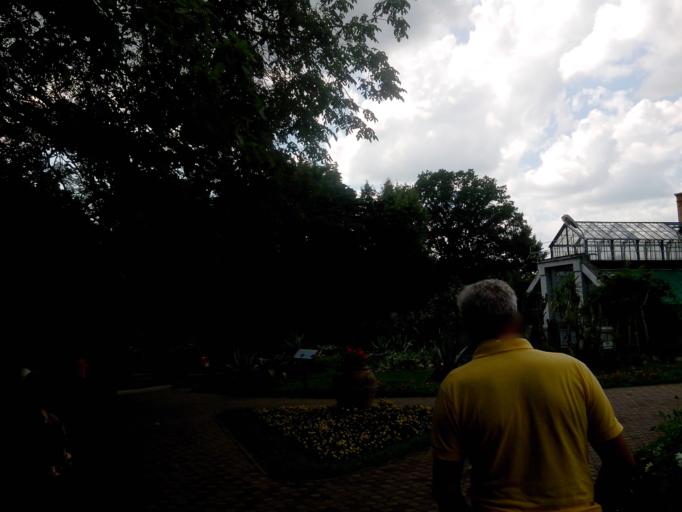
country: RO
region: Cluj
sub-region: Municipiul Cluj-Napoca
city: Cluj-Napoca
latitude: 46.7618
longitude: 23.5876
